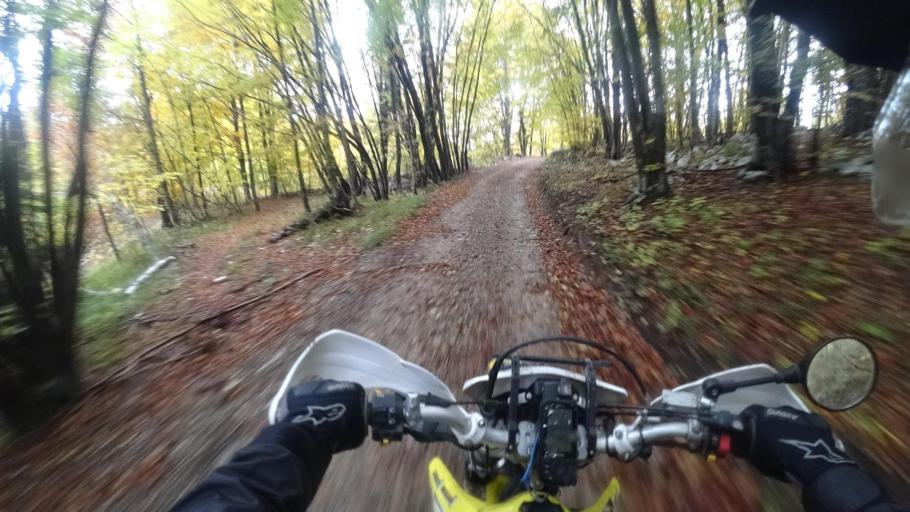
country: HR
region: Primorsko-Goranska
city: Vrbovsko
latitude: 45.4782
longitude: 15.0403
